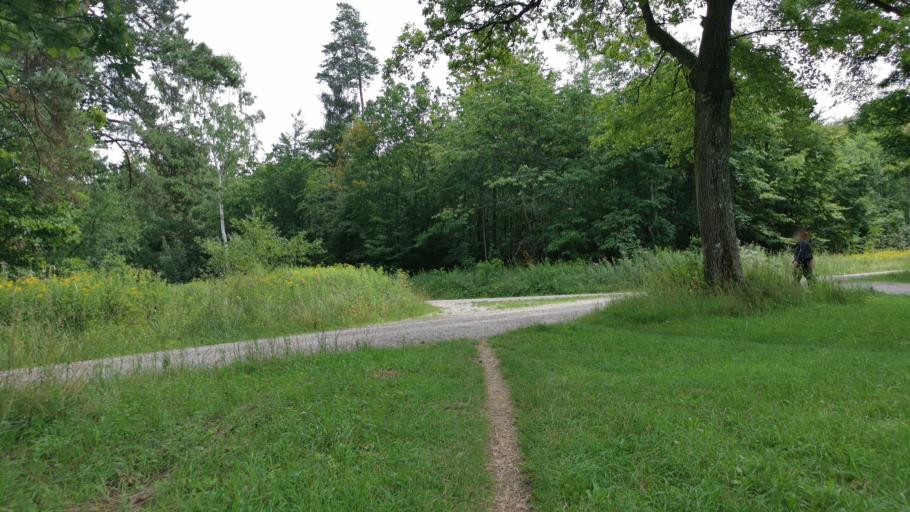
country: DE
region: Bavaria
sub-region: Upper Bavaria
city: Unterhaching
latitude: 48.0812
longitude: 11.5718
